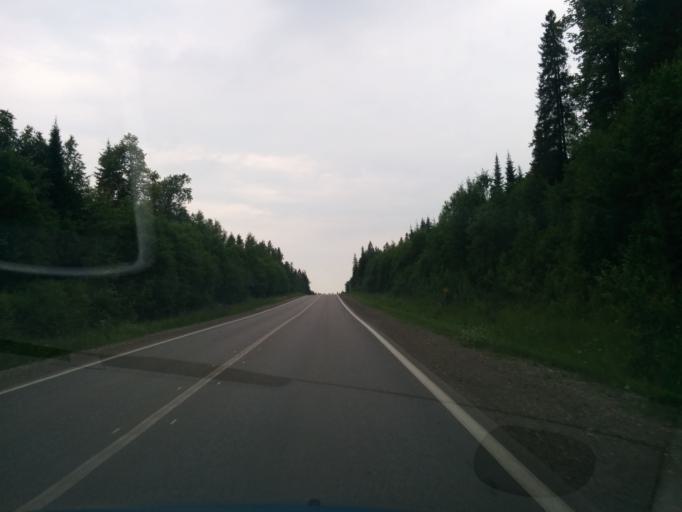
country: RU
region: Perm
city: Perm
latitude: 58.1920
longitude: 56.2139
